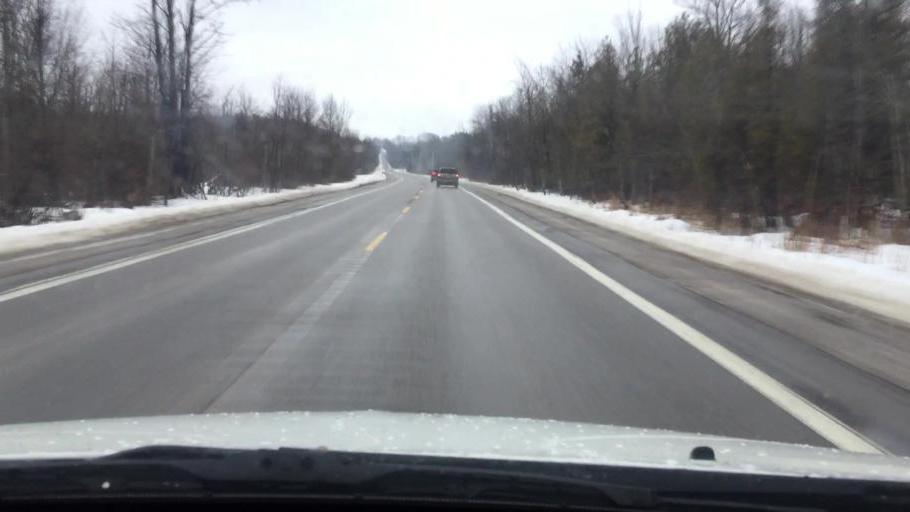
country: US
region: Michigan
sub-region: Charlevoix County
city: East Jordan
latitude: 45.2364
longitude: -85.1815
